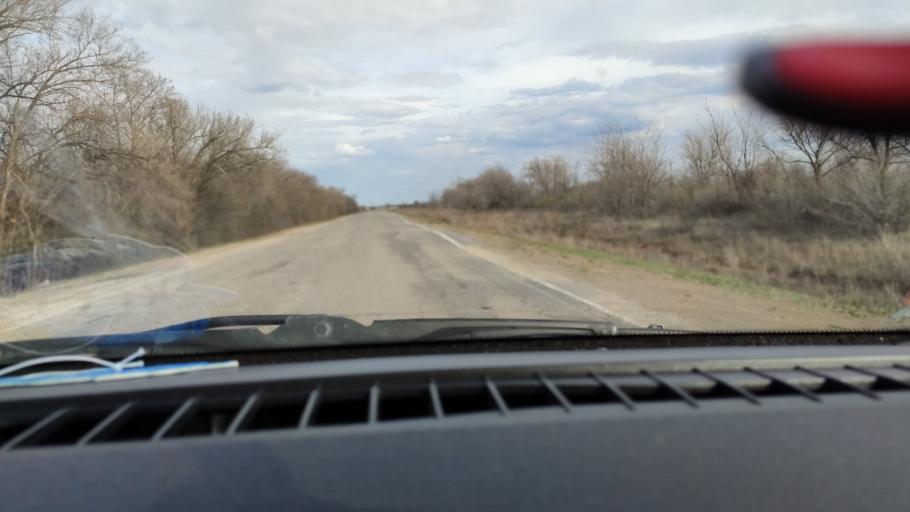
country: RU
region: Saratov
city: Rovnoye
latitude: 51.0662
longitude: 46.0053
